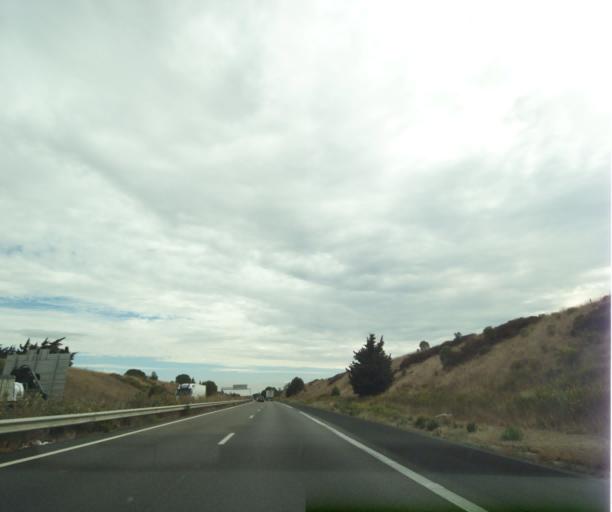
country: FR
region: Languedoc-Roussillon
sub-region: Departement du Gard
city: Garons
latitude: 43.7691
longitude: 4.4200
